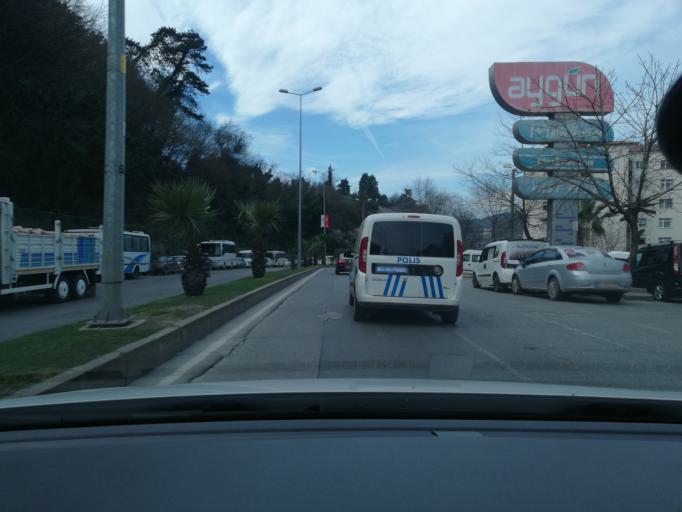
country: TR
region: Zonguldak
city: Eregli
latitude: 41.2761
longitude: 31.4245
